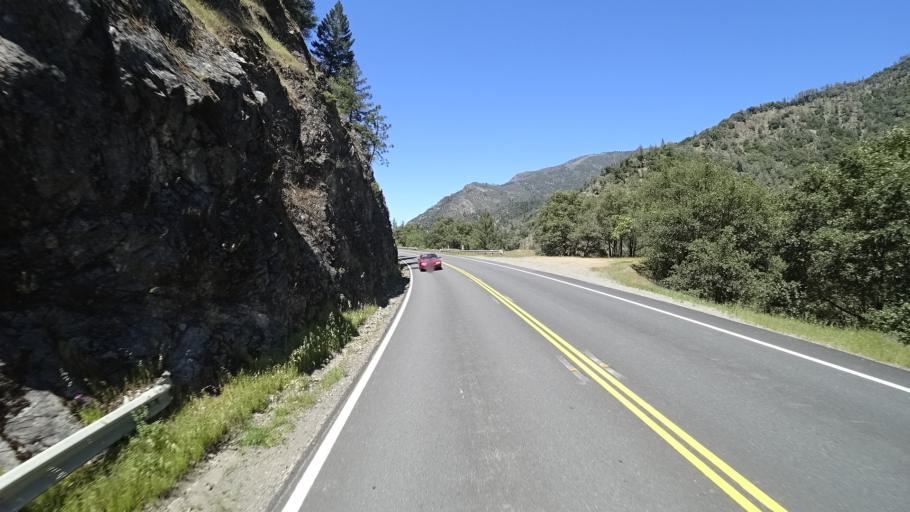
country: US
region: California
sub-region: Humboldt County
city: Willow Creek
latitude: 40.7925
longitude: -123.4560
